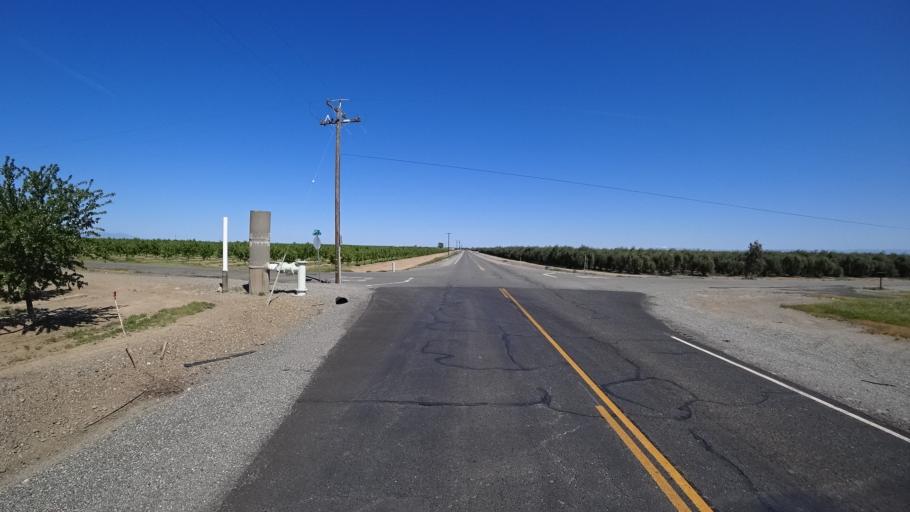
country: US
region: California
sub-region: Glenn County
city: Orland
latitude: 39.6814
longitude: -122.1404
